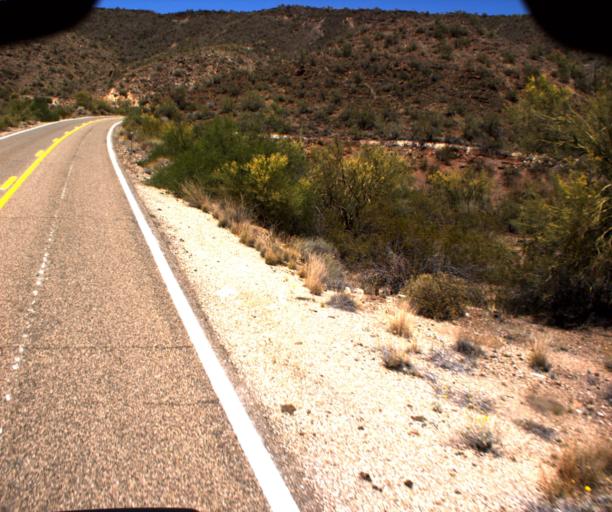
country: US
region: Arizona
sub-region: Yavapai County
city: Bagdad
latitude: 34.5018
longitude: -113.0689
